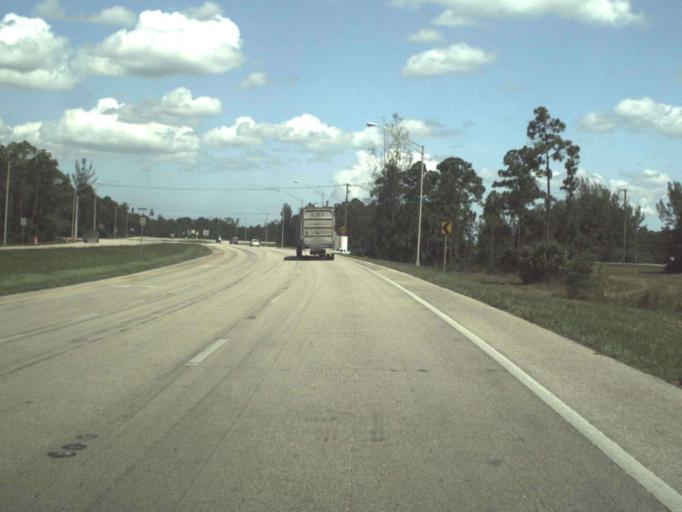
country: US
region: Florida
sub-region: Palm Beach County
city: Limestone Creek
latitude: 26.9037
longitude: -80.2928
